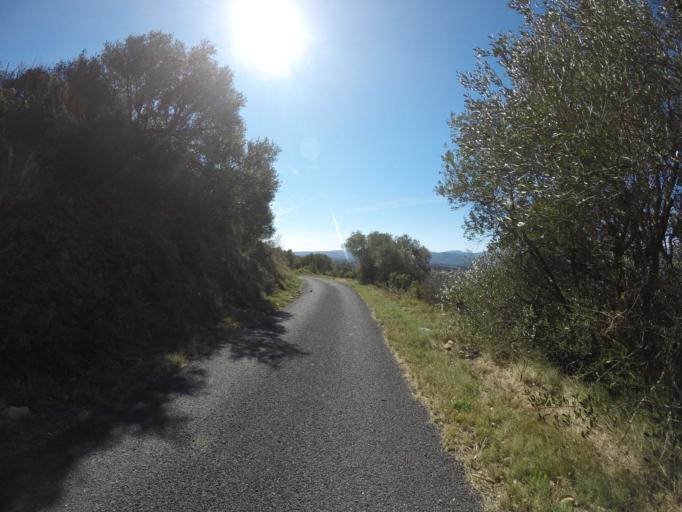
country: FR
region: Languedoc-Roussillon
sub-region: Departement des Pyrenees-Orientales
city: Millas
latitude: 42.7061
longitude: 2.6664
